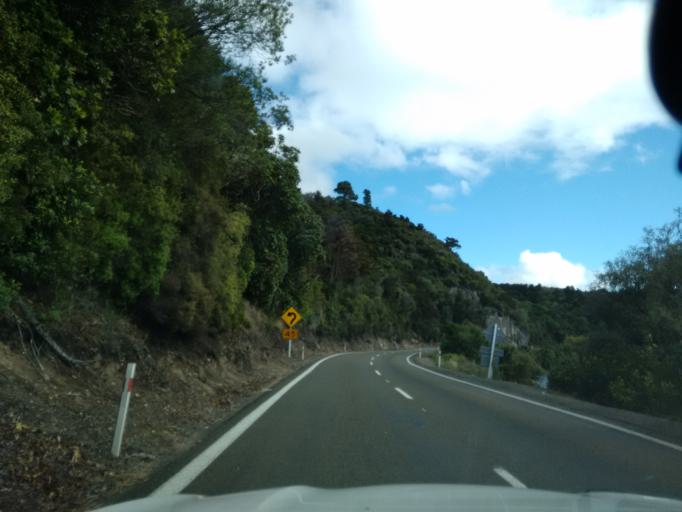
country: NZ
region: Waikato
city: Turangi
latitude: -38.8818
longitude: 175.9705
